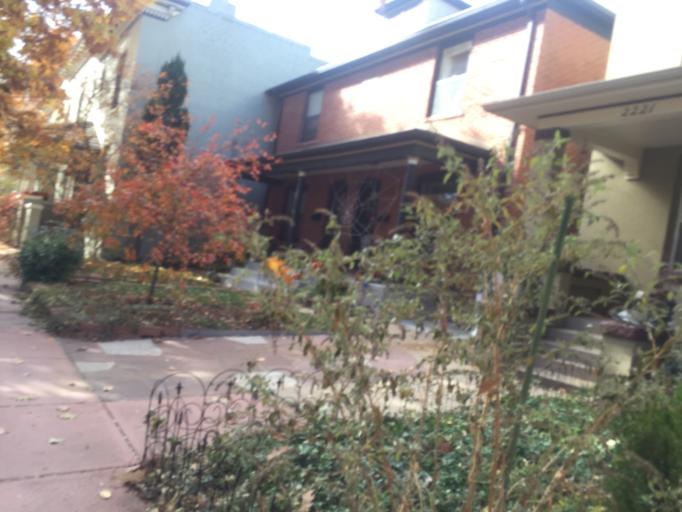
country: US
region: Colorado
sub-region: Denver County
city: Denver
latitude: 39.7502
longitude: -104.9759
